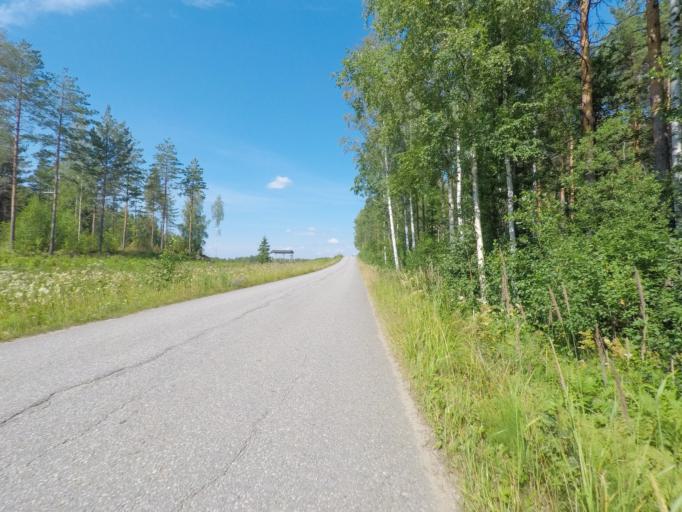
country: FI
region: Southern Savonia
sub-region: Mikkeli
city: Puumala
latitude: 61.4123
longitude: 28.0924
